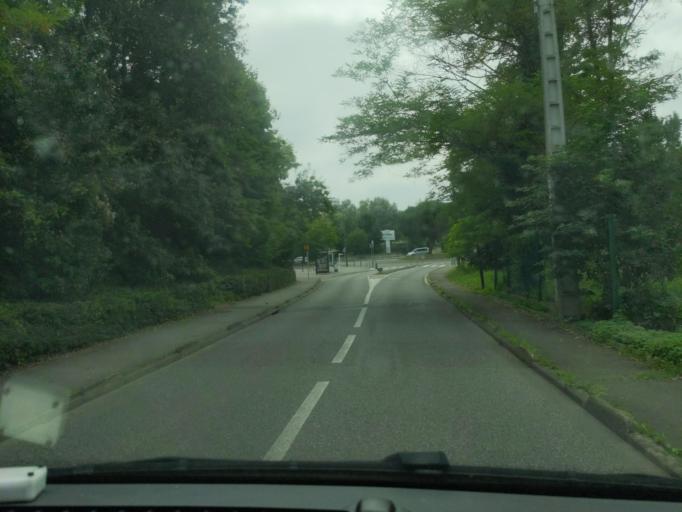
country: FR
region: Midi-Pyrenees
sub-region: Departement de la Haute-Garonne
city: Ramonville-Saint-Agne
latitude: 43.5555
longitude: 1.4570
